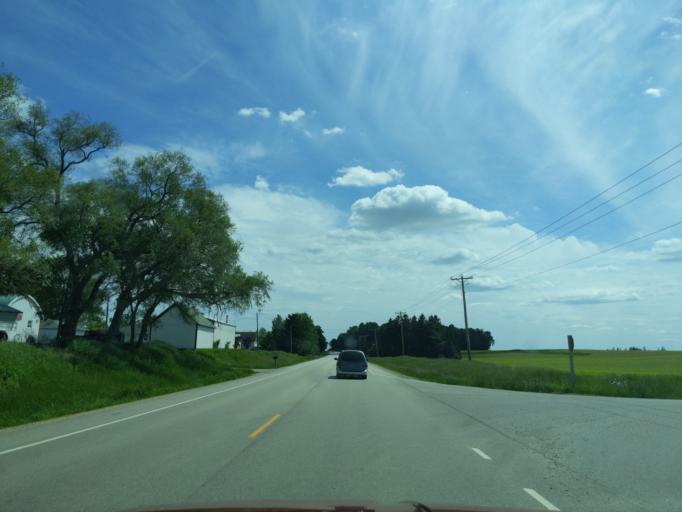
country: US
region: Wisconsin
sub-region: Columbia County
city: Poynette
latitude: 43.3544
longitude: -89.3286
